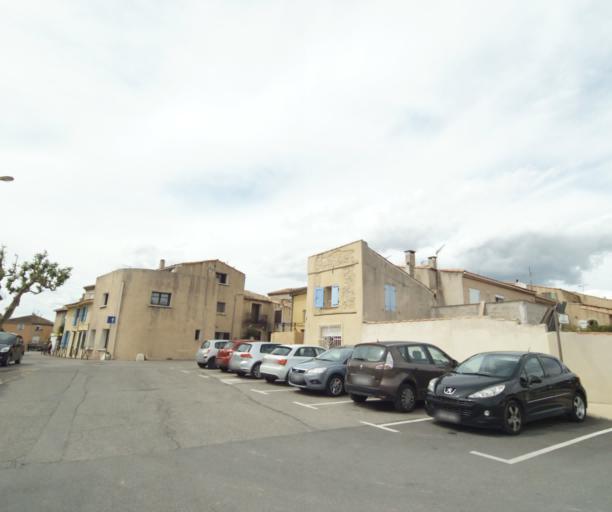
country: FR
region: Provence-Alpes-Cote d'Azur
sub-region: Departement des Bouches-du-Rhone
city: Rognac
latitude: 43.4875
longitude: 5.2353
